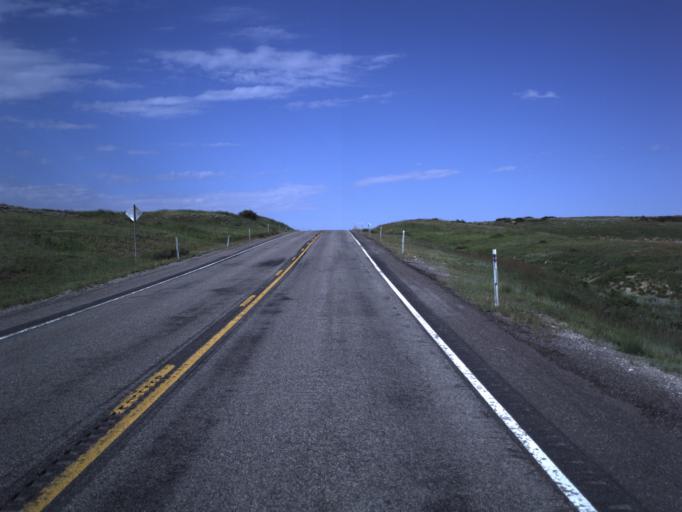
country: US
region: Utah
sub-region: Sanpete County
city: Fairview
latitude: 39.6190
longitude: -111.2974
